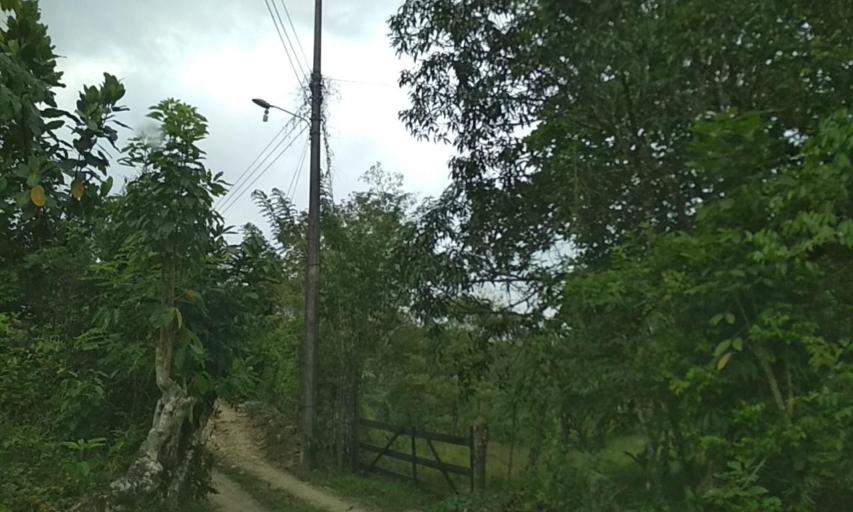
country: MX
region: Veracruz
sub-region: Uxpanapa
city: Poblado 10
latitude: 17.4600
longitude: -94.1049
